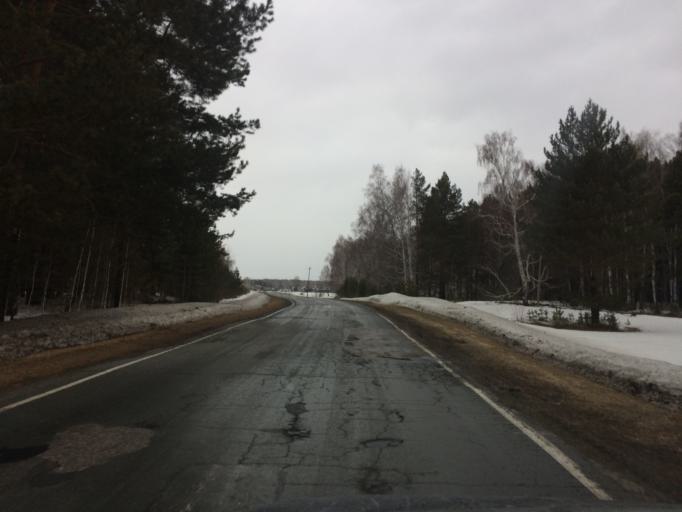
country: RU
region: Novosibirsk
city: Tashara
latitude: 55.4651
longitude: 83.4541
